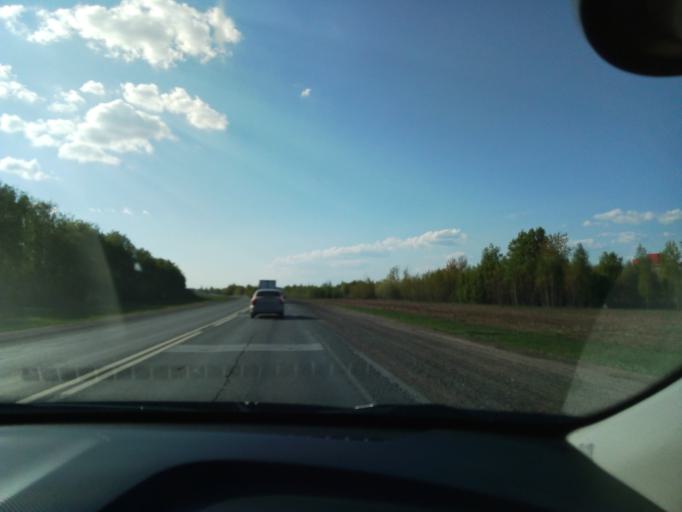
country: RU
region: Chuvashia
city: Kugesi
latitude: 56.0524
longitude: 47.2791
